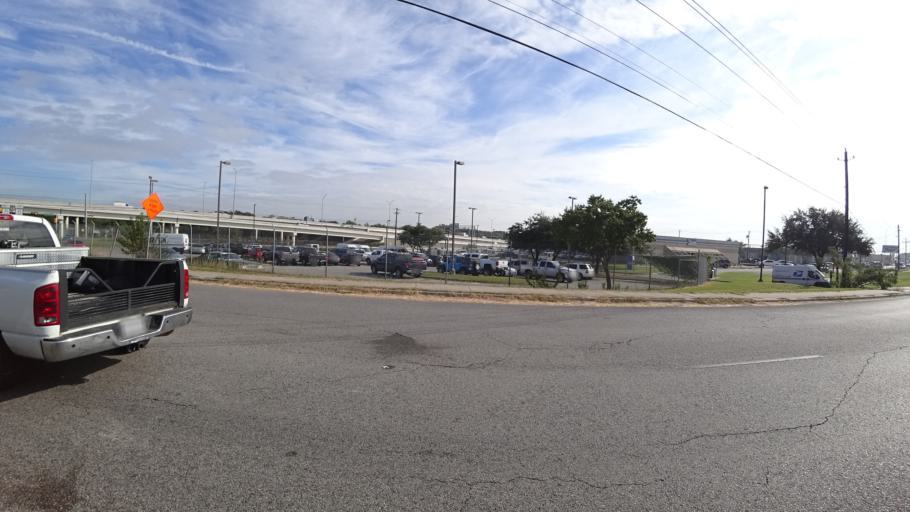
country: US
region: Texas
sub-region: Travis County
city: Austin
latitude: 30.2137
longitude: -97.7335
